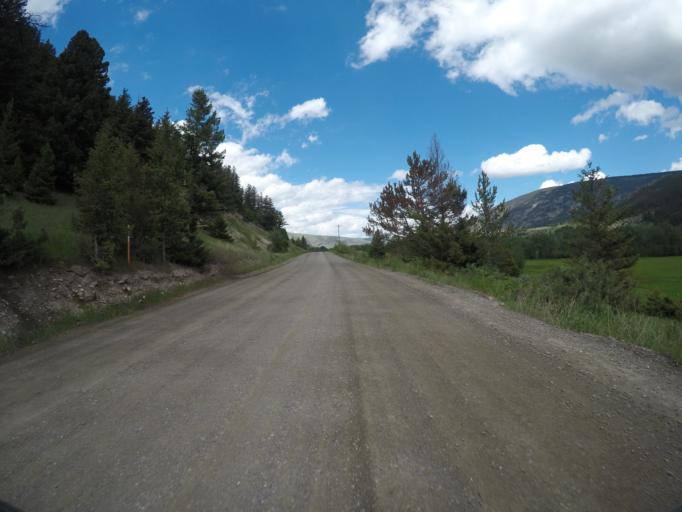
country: US
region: Montana
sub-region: Park County
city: Livingston
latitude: 45.5338
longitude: -110.2122
